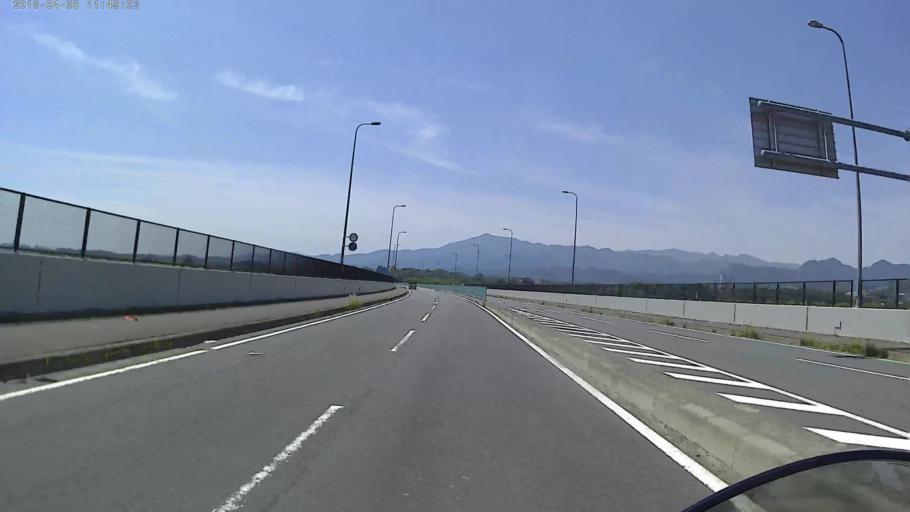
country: JP
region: Kanagawa
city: Zama
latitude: 35.4859
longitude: 139.3594
